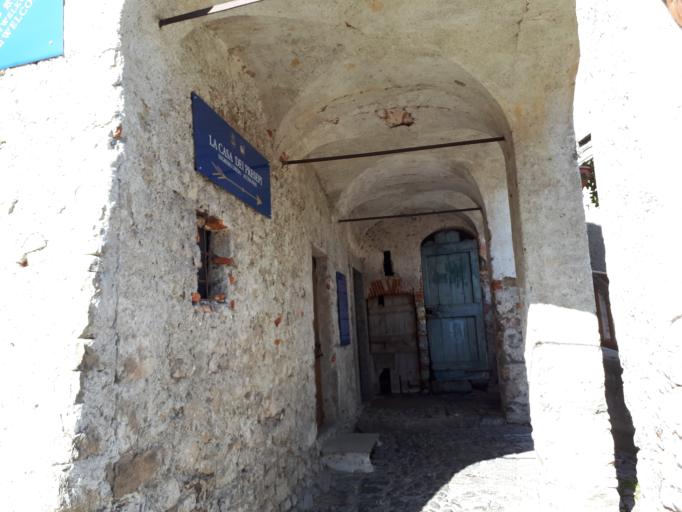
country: IT
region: Lombardy
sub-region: Provincia di Como
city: Mezzegra
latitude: 45.9834
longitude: 9.2045
